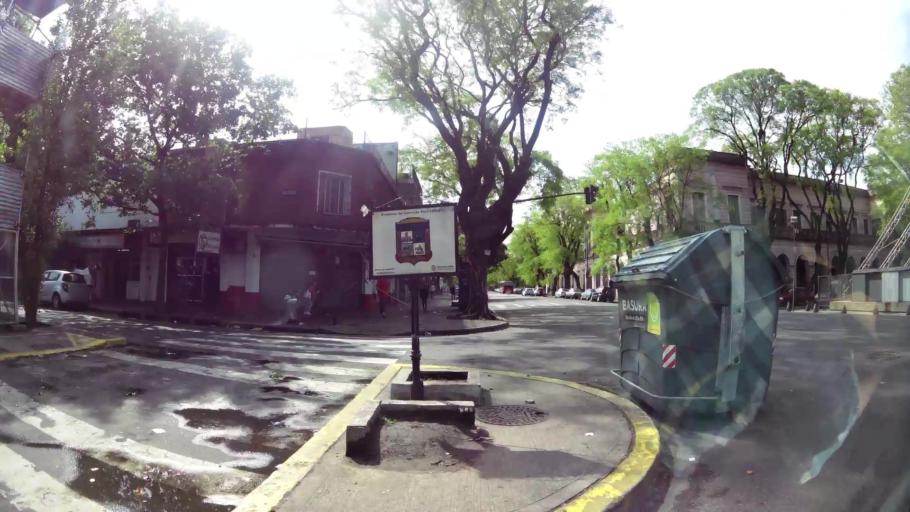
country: AR
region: Buenos Aires F.D.
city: Villa Lugano
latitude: -34.6626
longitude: -58.5003
